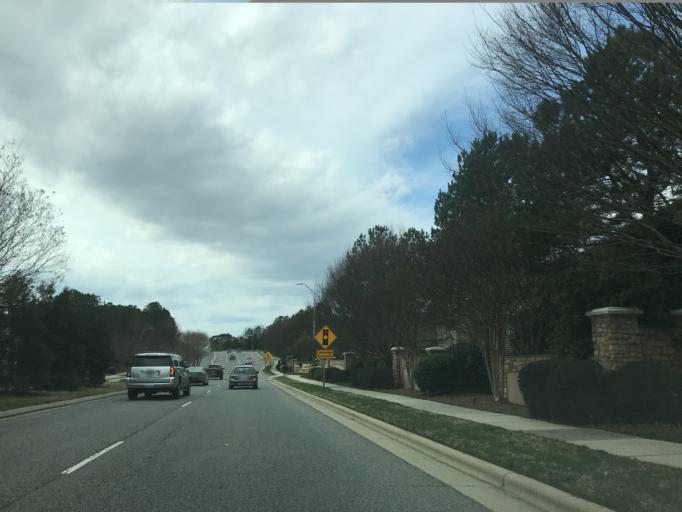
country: US
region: North Carolina
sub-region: Wake County
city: Morrisville
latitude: 35.7897
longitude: -78.8540
